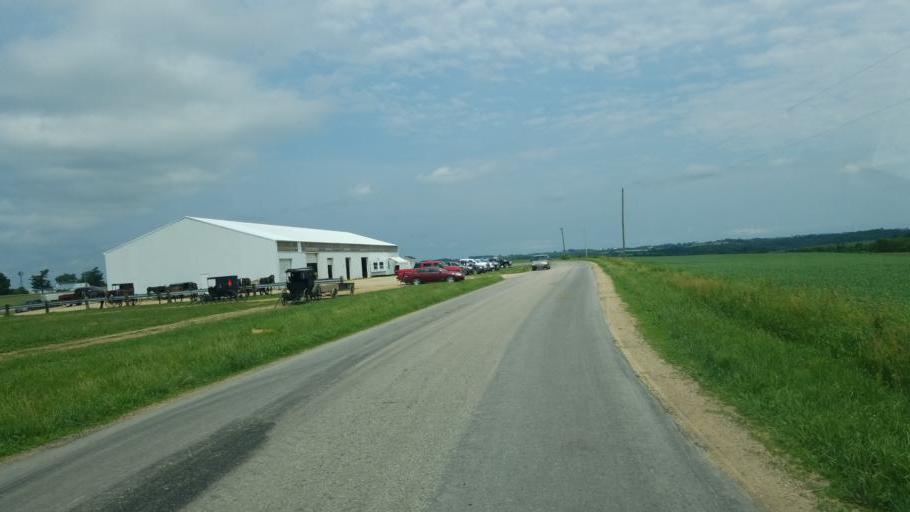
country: US
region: Wisconsin
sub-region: Monroe County
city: Cashton
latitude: 43.7150
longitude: -90.7204
